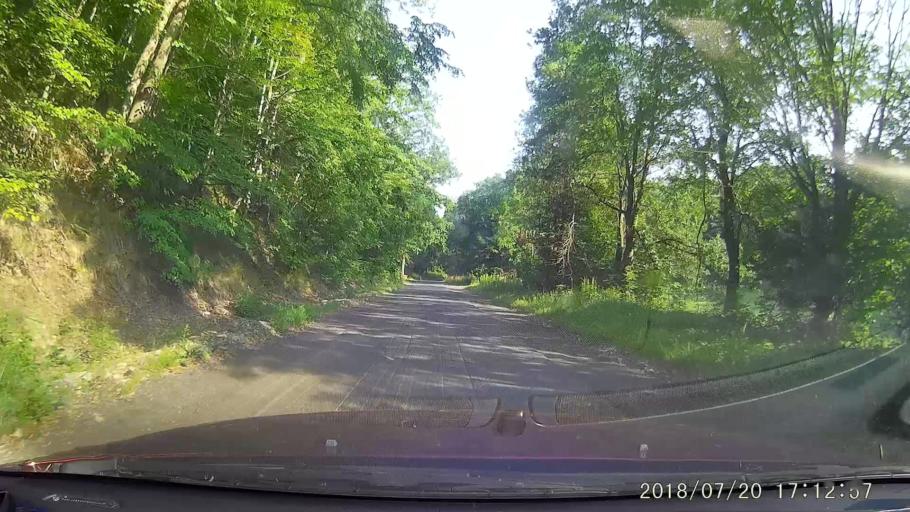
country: PL
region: Lower Silesian Voivodeship
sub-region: Powiat lubanski
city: Lesna
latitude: 51.0168
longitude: 15.2747
